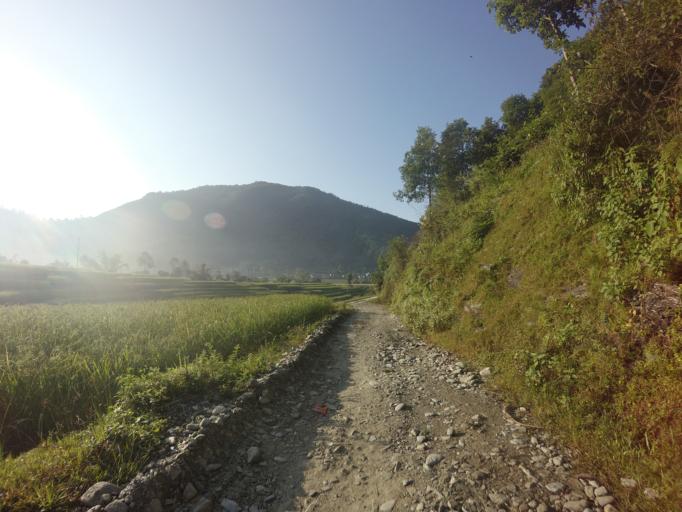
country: NP
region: Western Region
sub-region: Gandaki Zone
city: Pokhara
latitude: 28.2515
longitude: 84.0067
